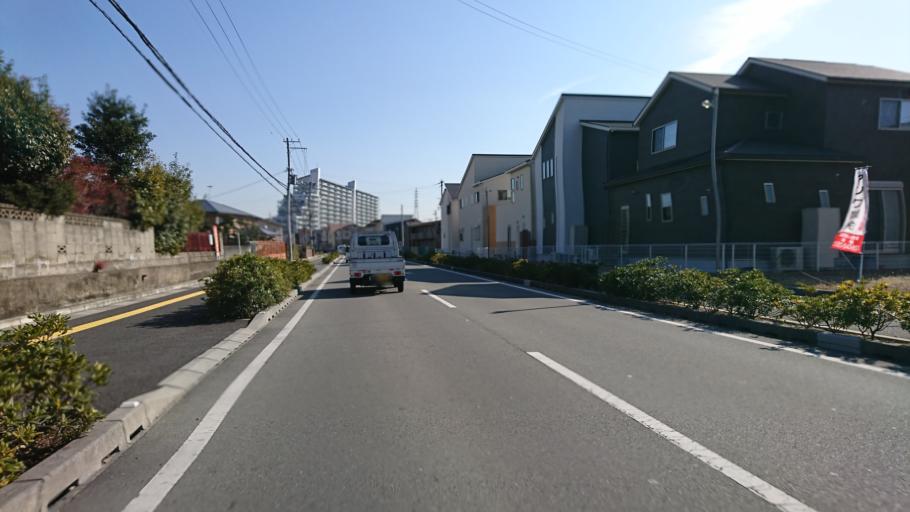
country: JP
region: Hyogo
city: Kakogawacho-honmachi
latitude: 34.7746
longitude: 134.8050
